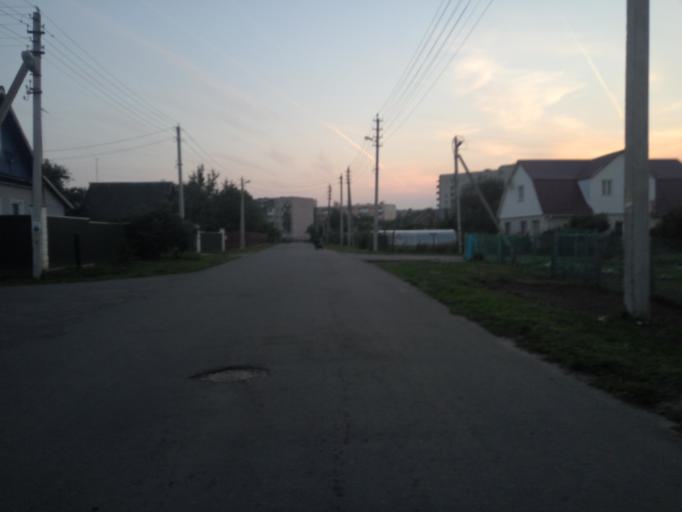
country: BY
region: Vitebsk
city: Vitebsk
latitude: 55.2024
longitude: 30.2486
